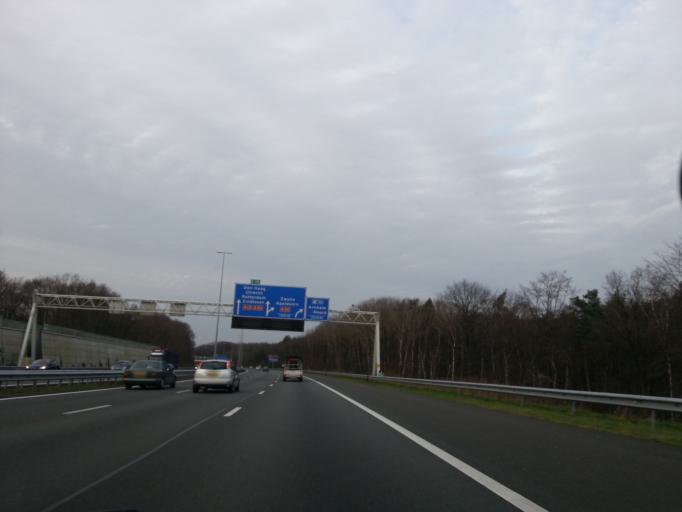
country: NL
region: Gelderland
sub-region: Gemeente Rozendaal
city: Rozendaal
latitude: 52.0047
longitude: 5.9486
